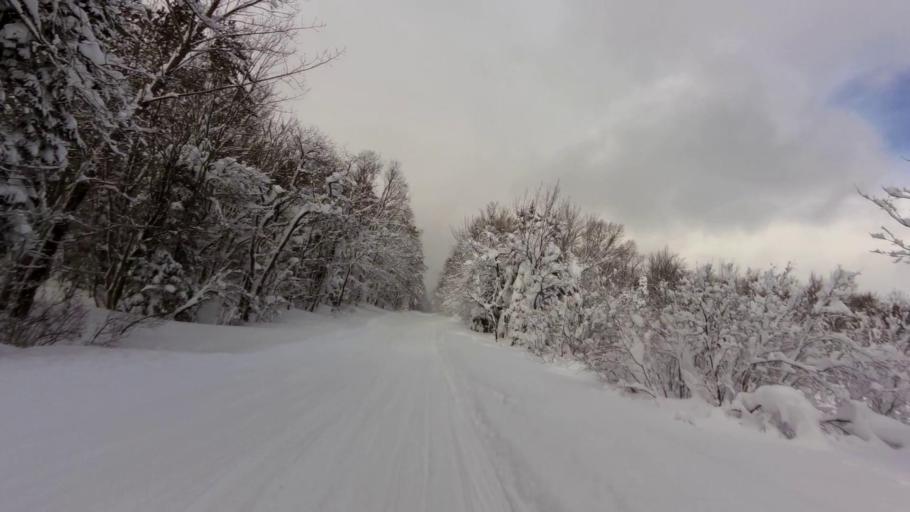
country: US
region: New York
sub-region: Lewis County
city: Lowville
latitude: 43.7481
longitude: -75.6751
